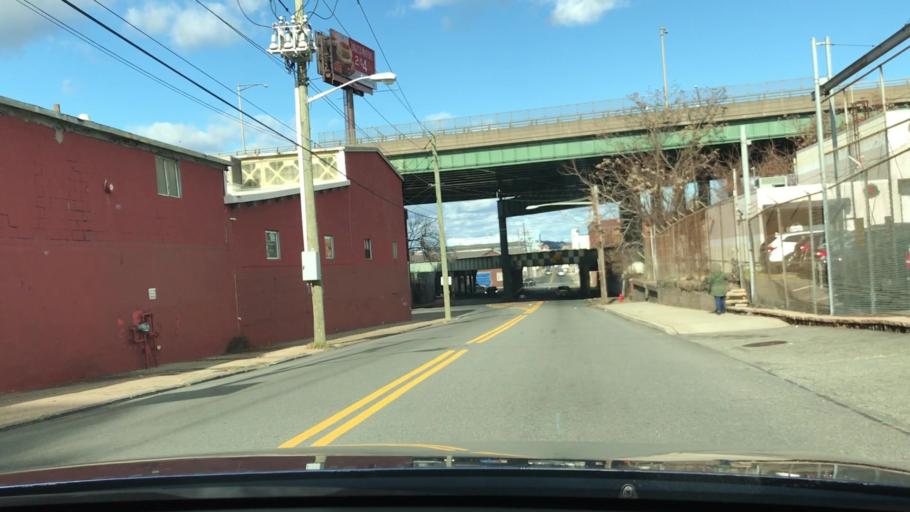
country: US
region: New Jersey
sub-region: Passaic County
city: Paterson
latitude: 40.9059
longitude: -74.1663
